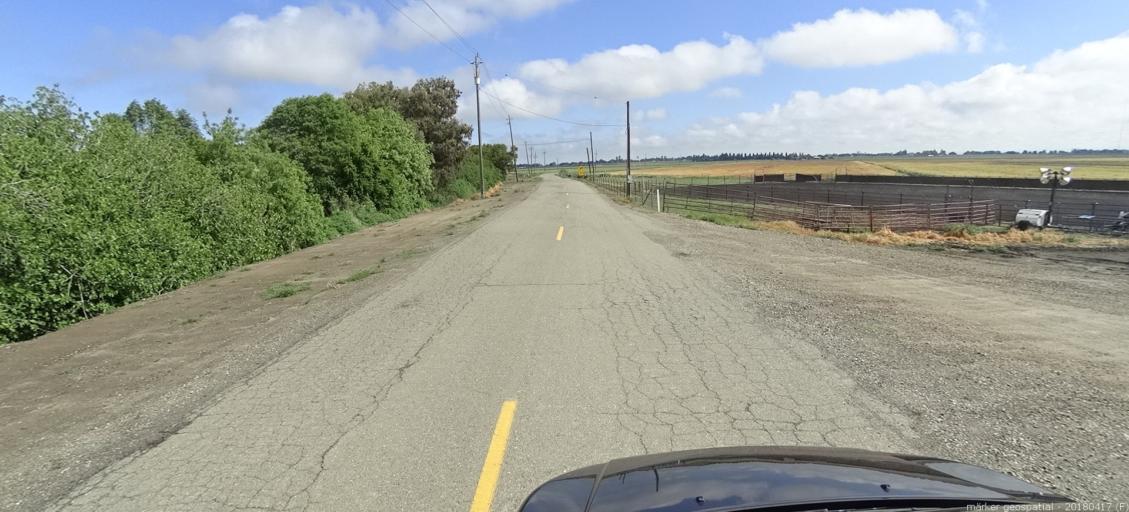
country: US
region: California
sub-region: Sacramento County
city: Walnut Grove
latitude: 38.2565
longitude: -121.5597
